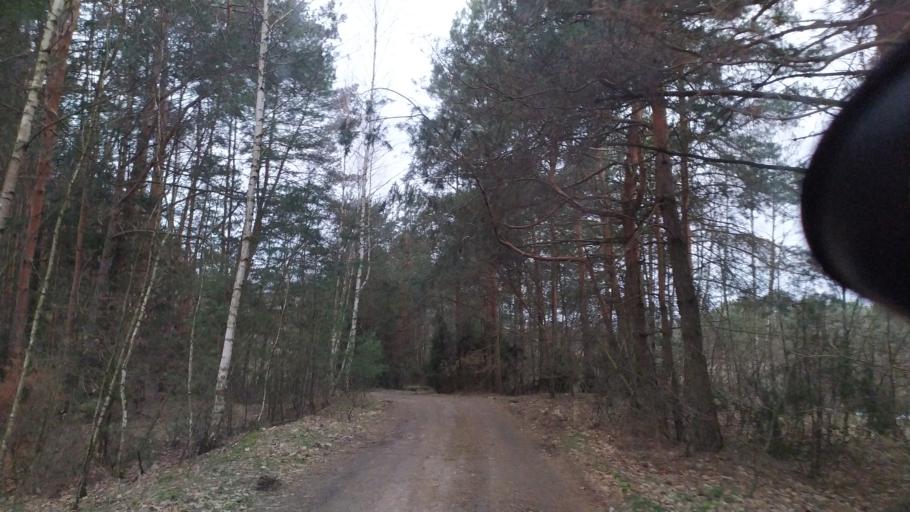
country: PL
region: Lublin Voivodeship
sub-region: Powiat lubartowski
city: Abramow
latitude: 51.4233
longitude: 22.2930
